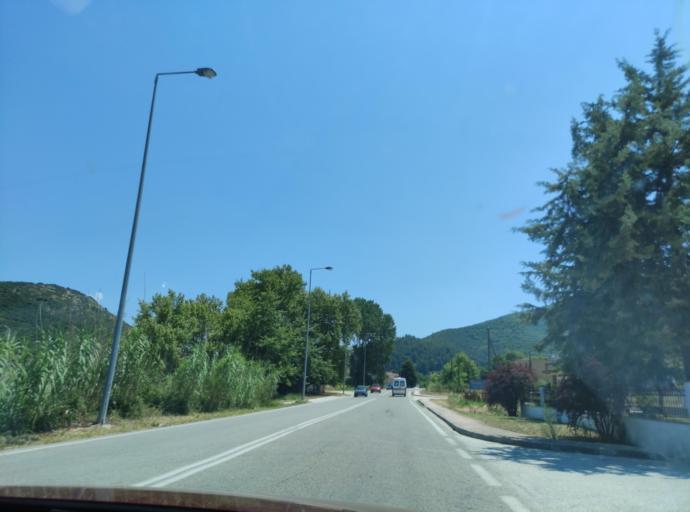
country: GR
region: East Macedonia and Thrace
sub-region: Nomos Kavalas
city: Palaiochori
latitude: 40.9512
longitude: 24.2044
